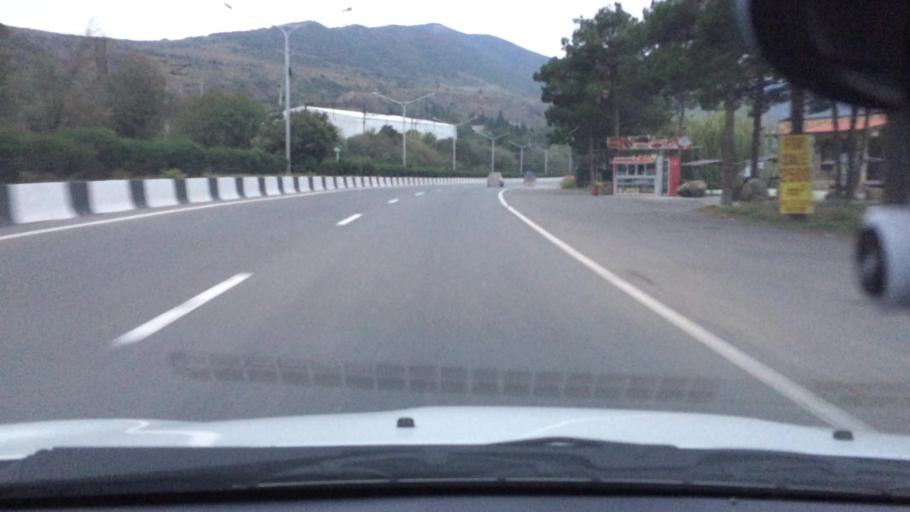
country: GE
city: Zahesi
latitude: 41.8186
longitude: 44.7479
